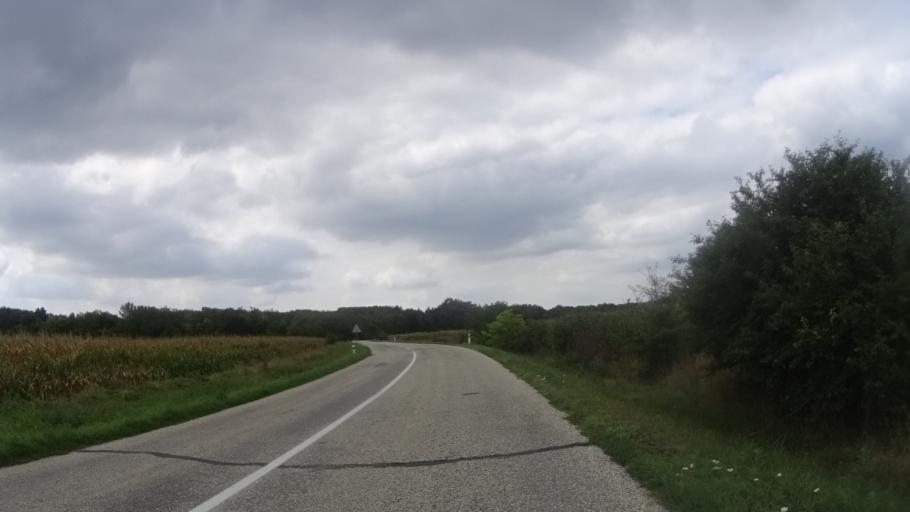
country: SK
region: Trnavsky
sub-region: Okres Dunajska Streda
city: Velky Meder
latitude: 47.7534
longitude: 17.8015
